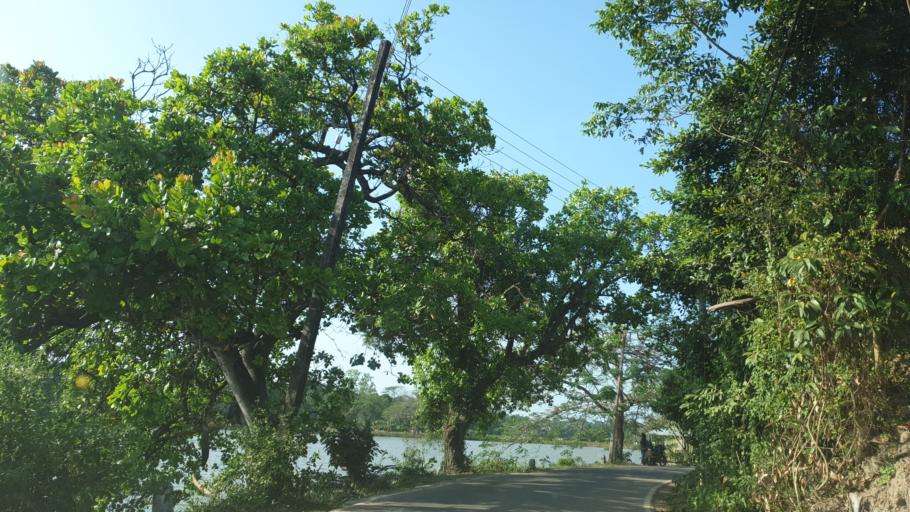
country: LK
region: Western
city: Battaramulla South
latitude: 6.8874
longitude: 79.9479
